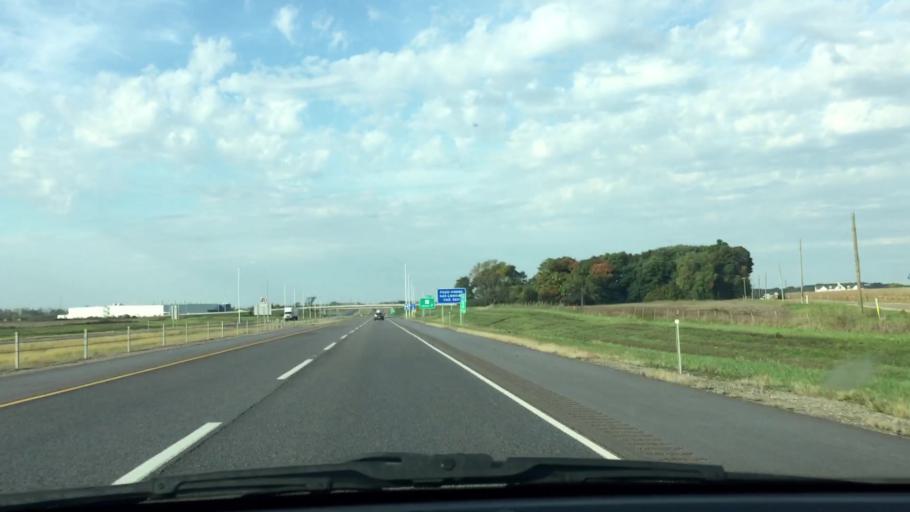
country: US
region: Illinois
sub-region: Lee County
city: Dixon
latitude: 41.8231
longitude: -89.4577
